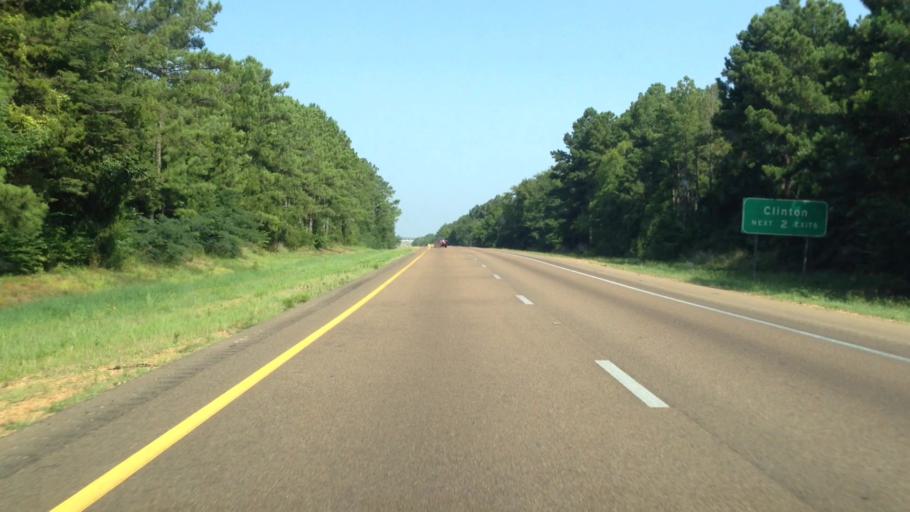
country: US
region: Mississippi
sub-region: Hinds County
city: Clinton
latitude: 32.3118
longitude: -90.2985
